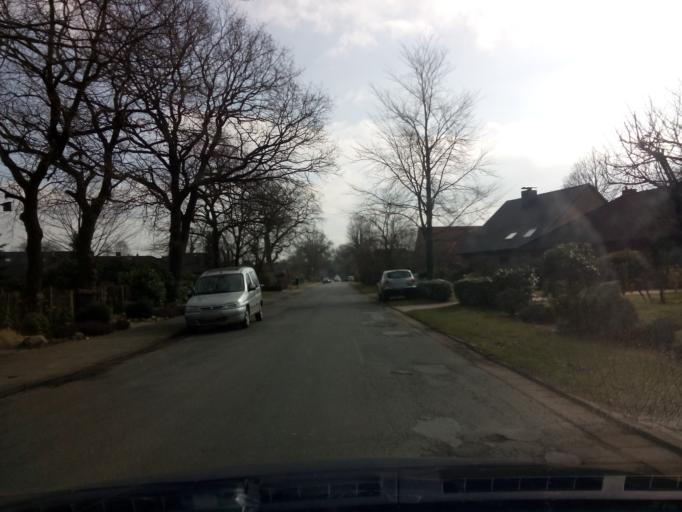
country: DE
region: Lower Saxony
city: Osterholz-Scharmbeck
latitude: 53.2294
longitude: 8.7574
